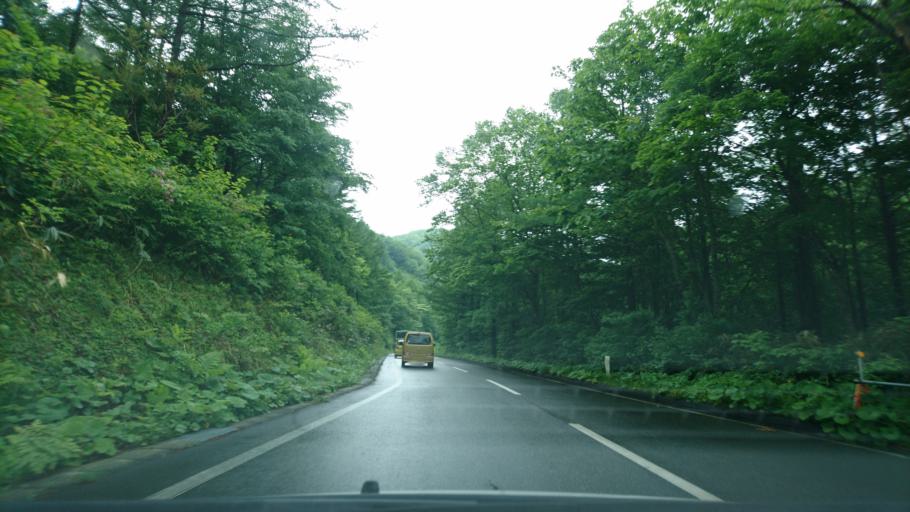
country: JP
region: Iwate
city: Ichinoseki
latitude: 38.9940
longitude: 140.8249
